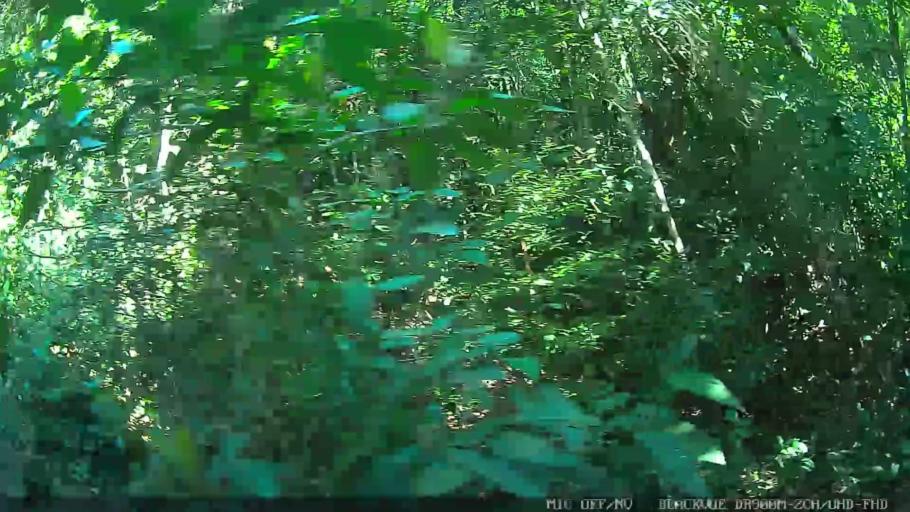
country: BR
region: Sao Paulo
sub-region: Guaruja
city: Guaruja
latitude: -23.9810
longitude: -46.2551
